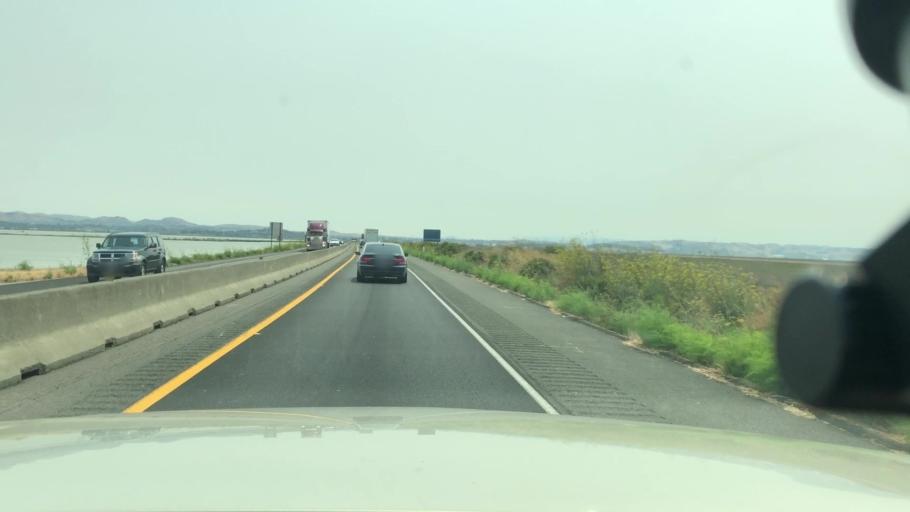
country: US
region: California
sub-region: Solano County
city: Vallejo
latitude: 38.1340
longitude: -122.3429
